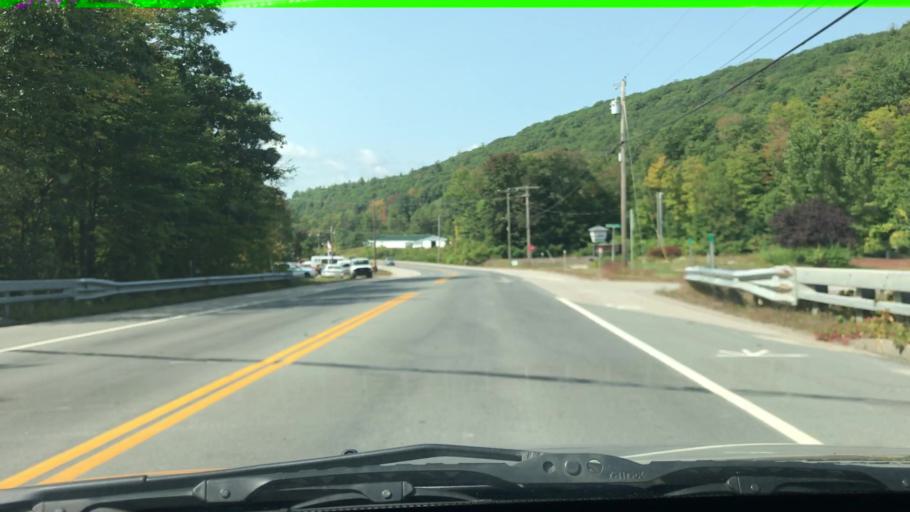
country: US
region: New Hampshire
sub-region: Cheshire County
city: Marlborough
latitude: 42.8724
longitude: -72.2153
